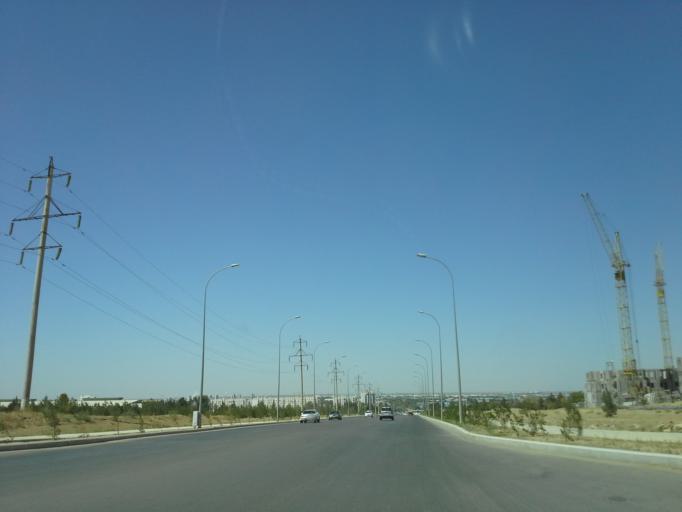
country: TM
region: Ahal
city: Ashgabat
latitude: 37.8964
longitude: 58.4057
